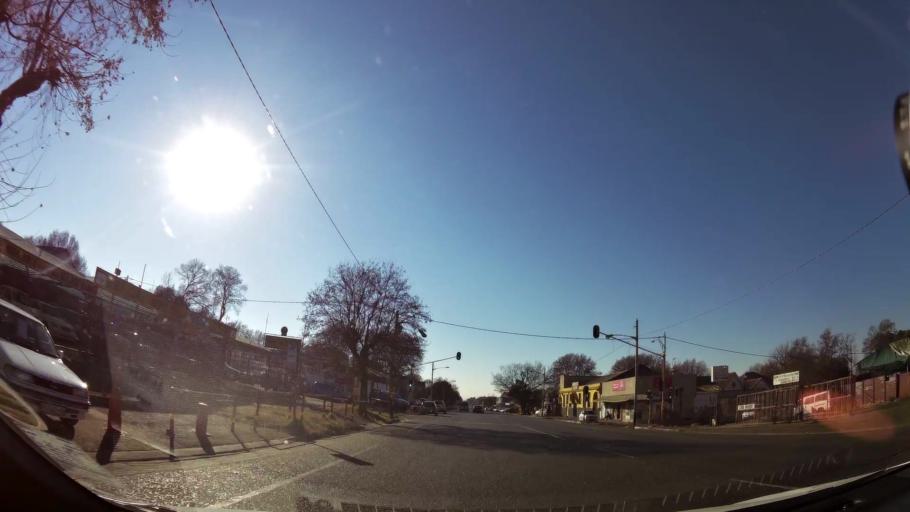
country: ZA
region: Gauteng
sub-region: City of Johannesburg Metropolitan Municipality
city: Johannesburg
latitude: -26.2054
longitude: 28.0799
